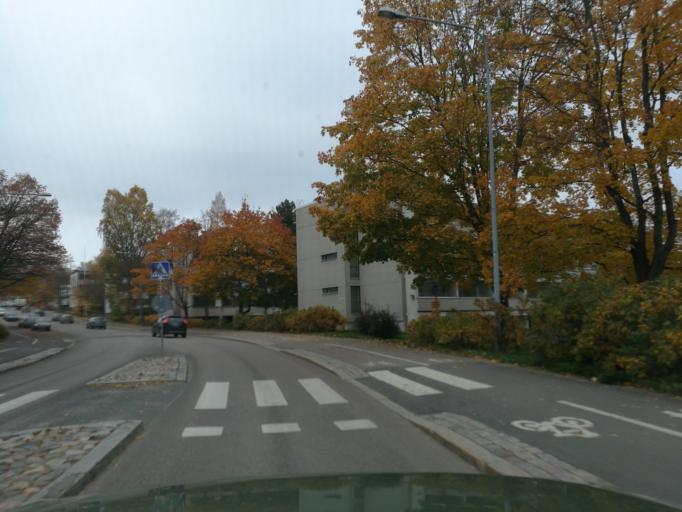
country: FI
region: Uusimaa
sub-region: Helsinki
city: Helsinki
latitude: 60.2315
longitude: 24.9678
